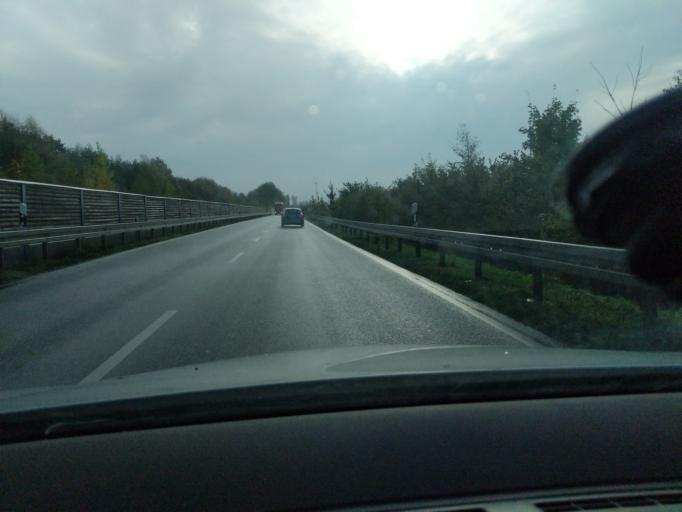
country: DE
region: Lower Saxony
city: Neu Wulmstorf
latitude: 53.5150
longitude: 9.8334
